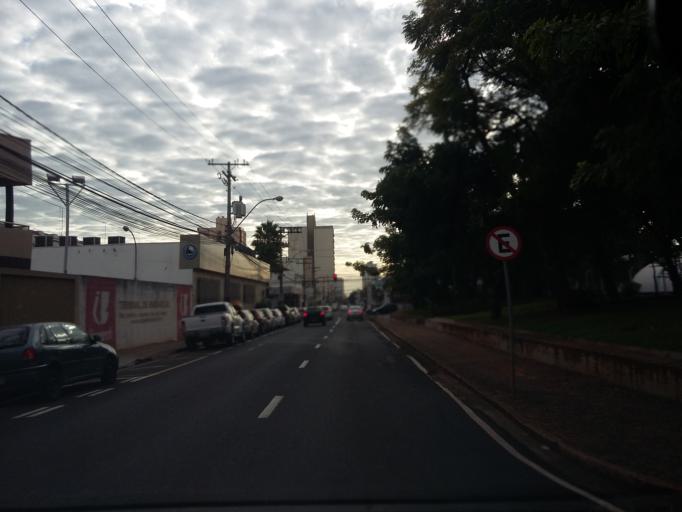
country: BR
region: Sao Paulo
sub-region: Sao Jose Do Rio Preto
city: Sao Jose do Rio Preto
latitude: -20.8218
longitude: -49.3918
